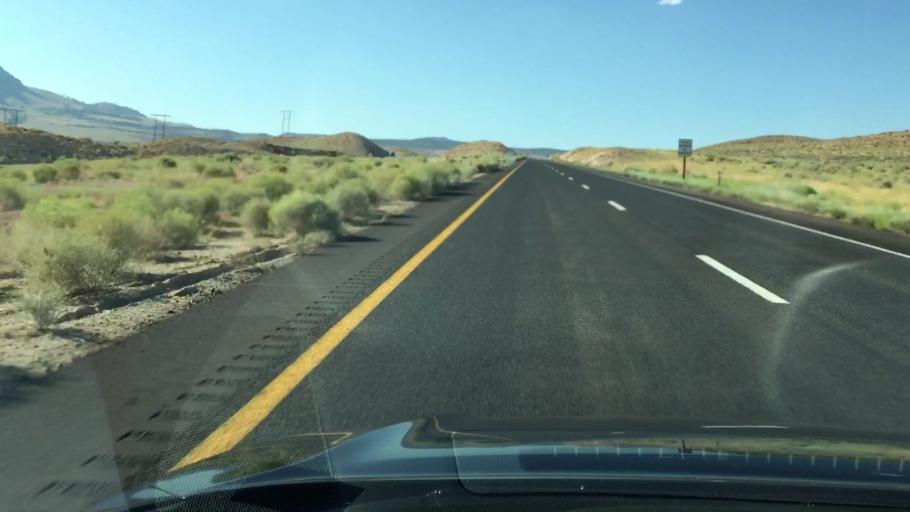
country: US
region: California
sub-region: Inyo County
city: West Bishop
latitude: 37.4581
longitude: -118.5757
